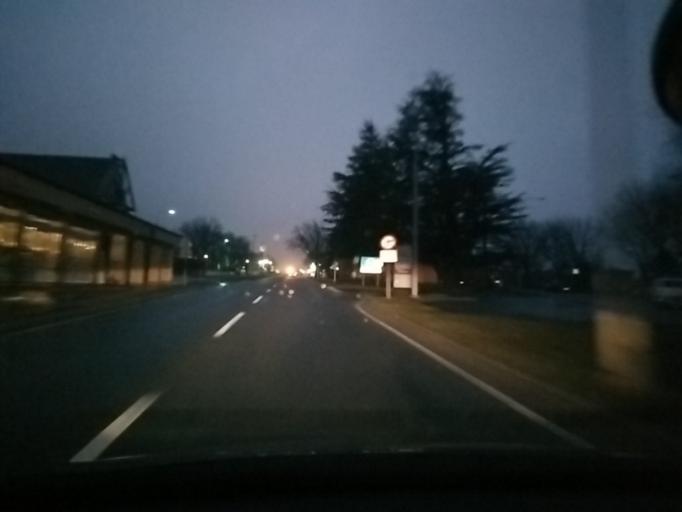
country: SI
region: Hrpelje-Kozina
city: Kozina
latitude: 45.6213
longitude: 13.9057
